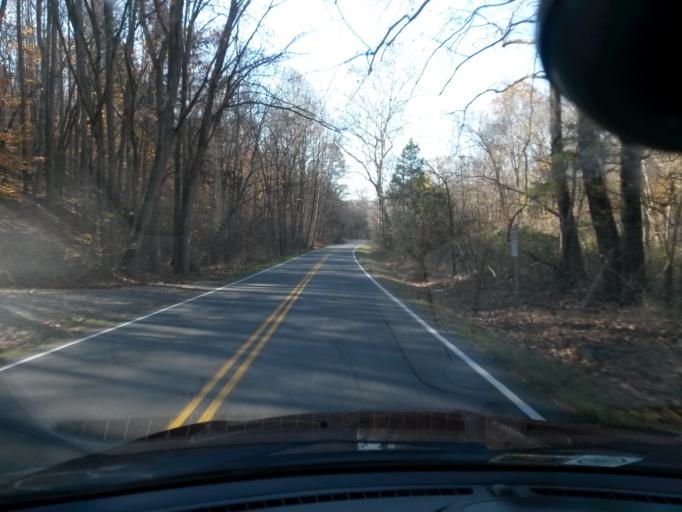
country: US
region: Virginia
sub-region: Botetourt County
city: Buchanan
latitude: 37.6195
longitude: -79.7349
